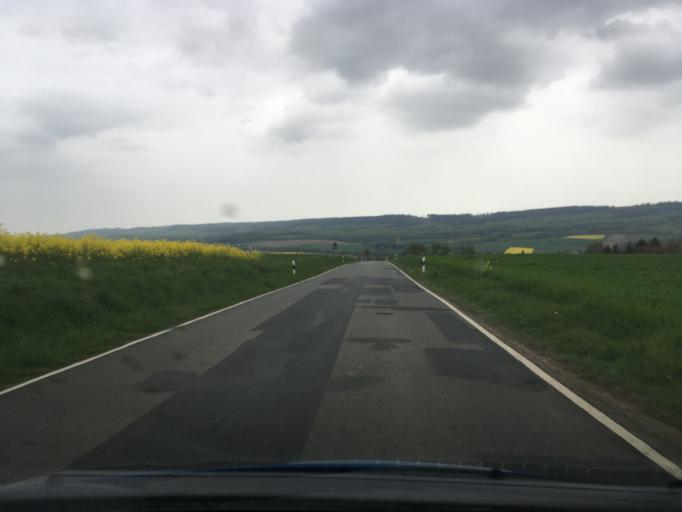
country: DE
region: Lower Saxony
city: Eimen
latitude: 51.8569
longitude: 9.8098
